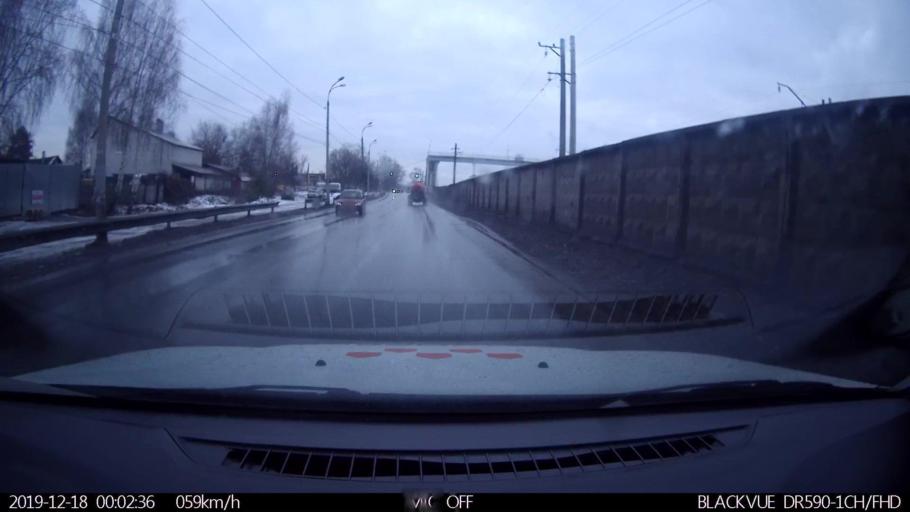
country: RU
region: Nizjnij Novgorod
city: Gorbatovka
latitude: 56.3669
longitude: 43.8296
